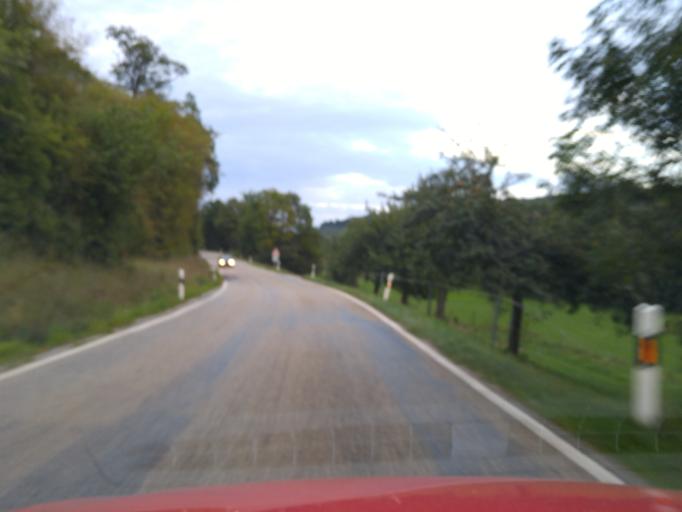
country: DE
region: Baden-Wuerttemberg
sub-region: Regierungsbezirk Stuttgart
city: Zaberfeld
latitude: 49.0187
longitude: 8.9363
